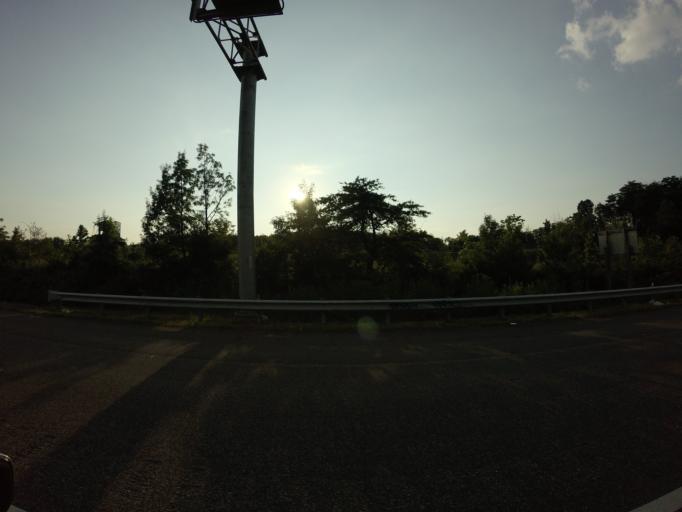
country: US
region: Maryland
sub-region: Prince George's County
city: West Laurel
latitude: 39.0922
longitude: -76.8925
